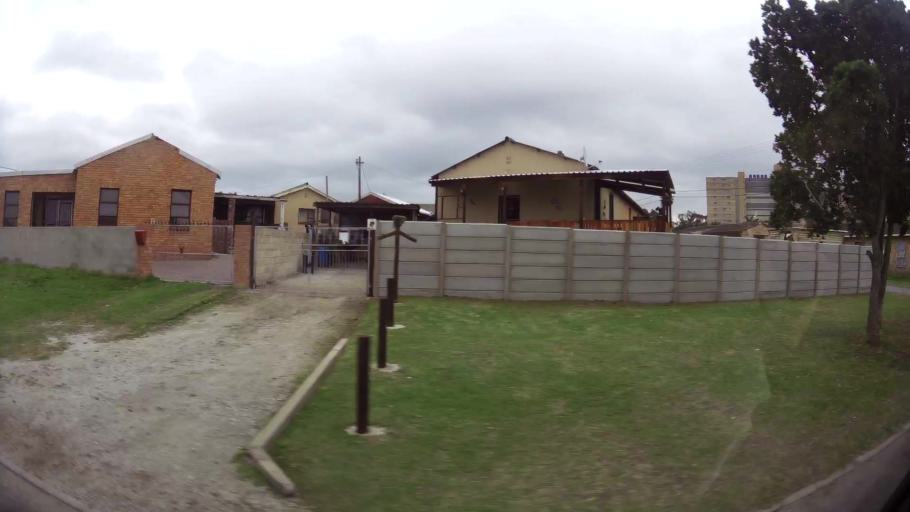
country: ZA
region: Eastern Cape
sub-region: Nelson Mandela Bay Metropolitan Municipality
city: Port Elizabeth
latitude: -33.9042
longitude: 25.5703
